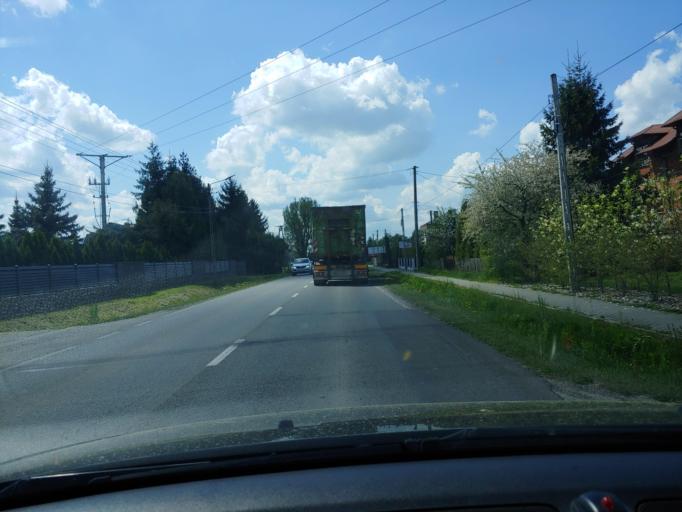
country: PL
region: Subcarpathian Voivodeship
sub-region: Powiat mielecki
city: Mielec
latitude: 50.2803
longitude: 21.3864
